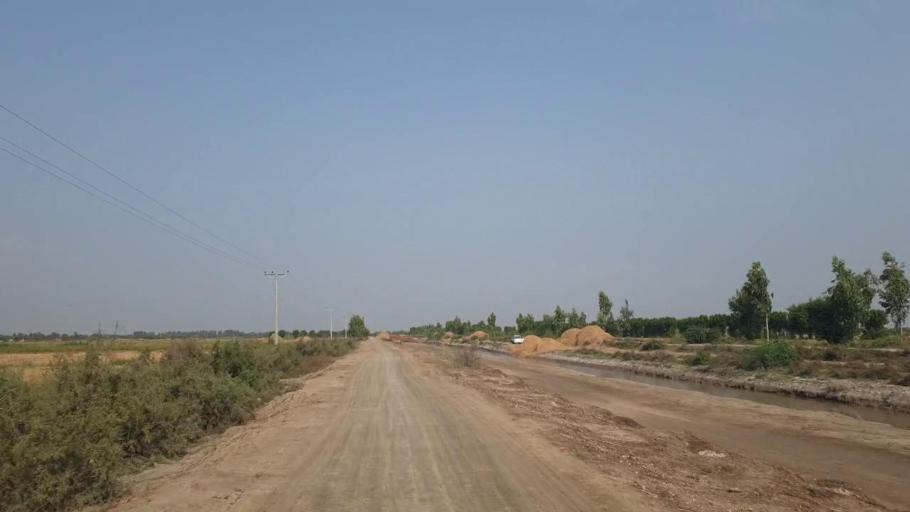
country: PK
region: Sindh
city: Badin
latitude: 24.7464
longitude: 68.7632
